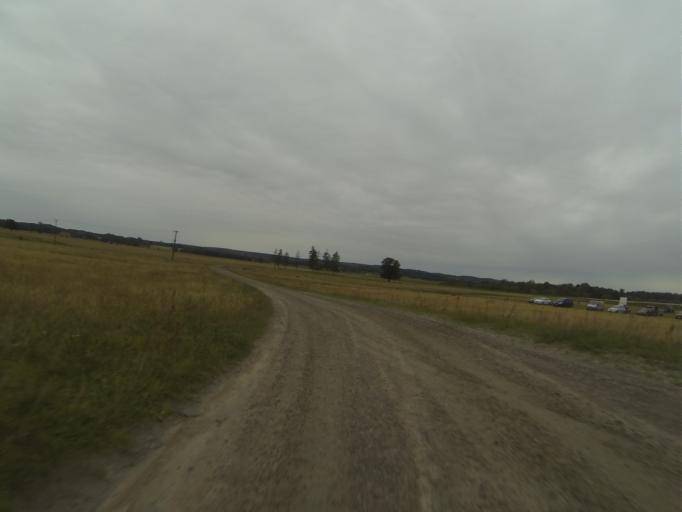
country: SE
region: Skane
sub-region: Lunds Kommun
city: Veberod
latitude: 55.7141
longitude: 13.4236
